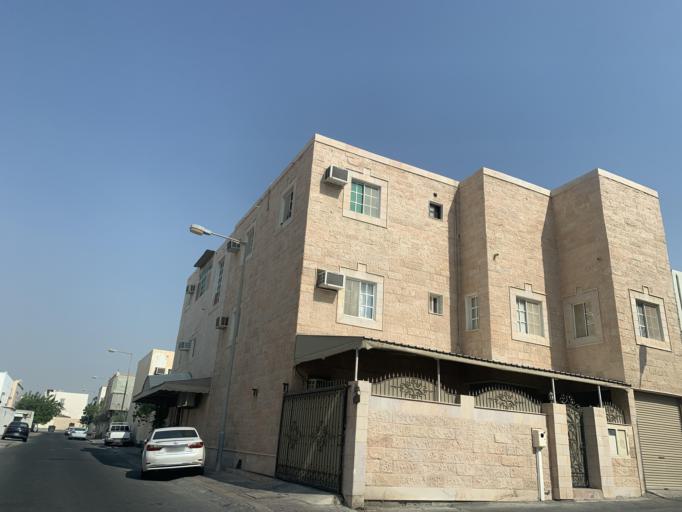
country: BH
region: Central Governorate
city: Madinat Hamad
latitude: 26.1257
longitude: 50.4949
